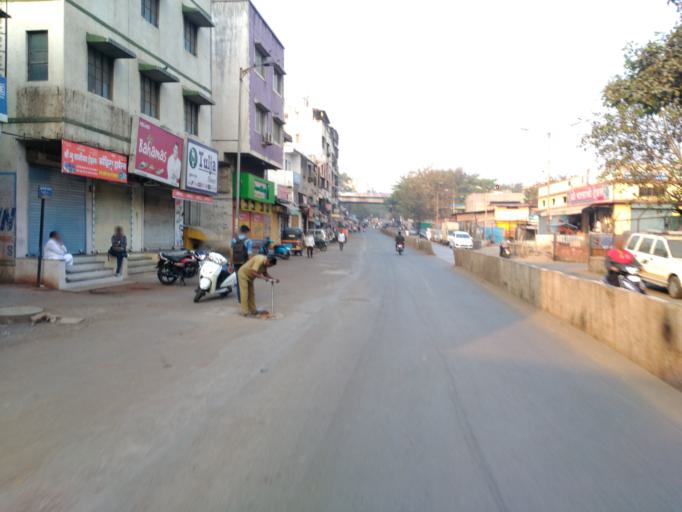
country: IN
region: Maharashtra
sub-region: Pune Division
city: Pune
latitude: 18.4687
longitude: 73.8595
